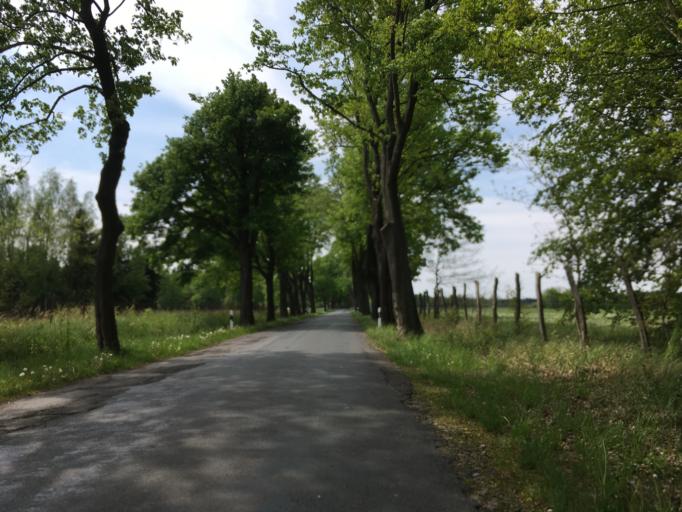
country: DE
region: Brandenburg
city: Melchow
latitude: 52.7428
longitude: 13.6817
